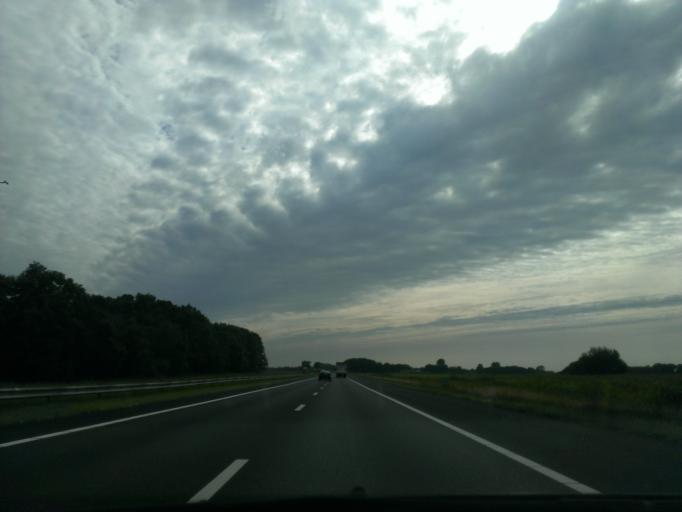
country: NL
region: Drenthe
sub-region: Gemeente Hoogeveen
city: Hoogeveen
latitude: 52.6987
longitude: 6.4131
